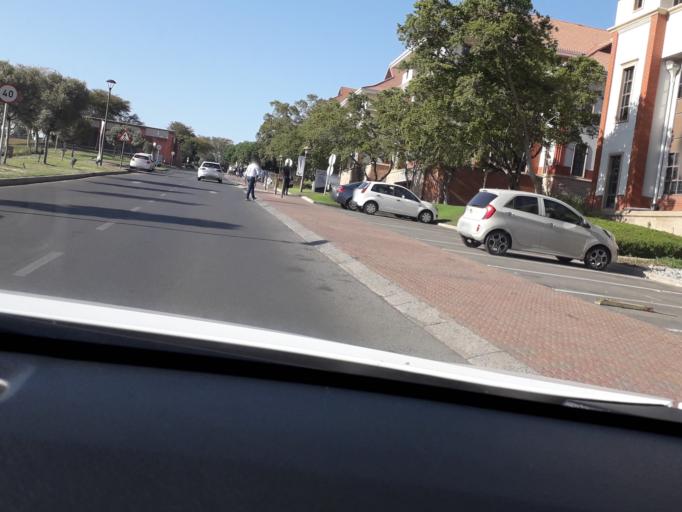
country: ZA
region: Gauteng
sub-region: City of Johannesburg Metropolitan Municipality
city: Diepsloot
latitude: -26.0416
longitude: 28.0244
